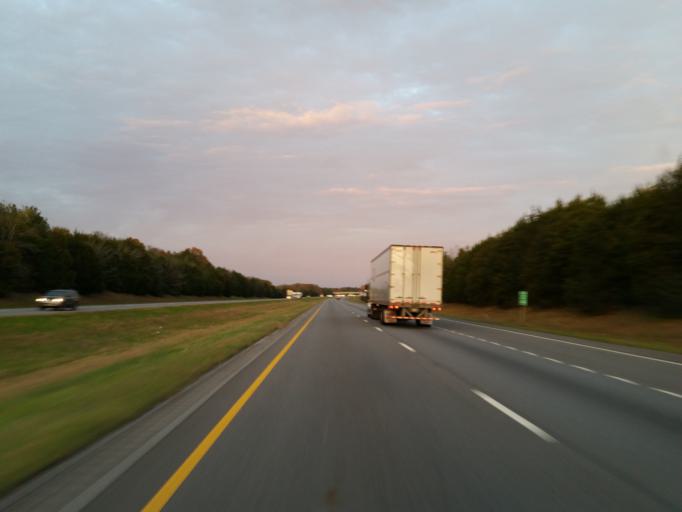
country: US
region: Alabama
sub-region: Sumter County
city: Livingston
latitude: 32.7057
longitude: -88.1374
